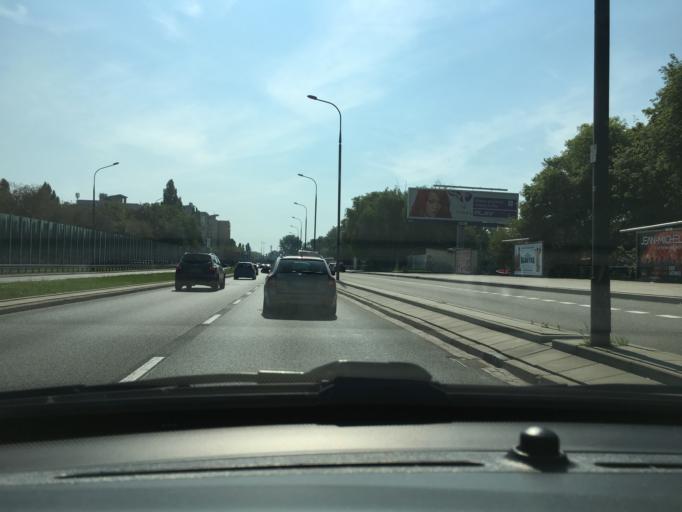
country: PL
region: Masovian Voivodeship
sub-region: Warszawa
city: Praga Polnoc
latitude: 52.2324
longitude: 21.0486
